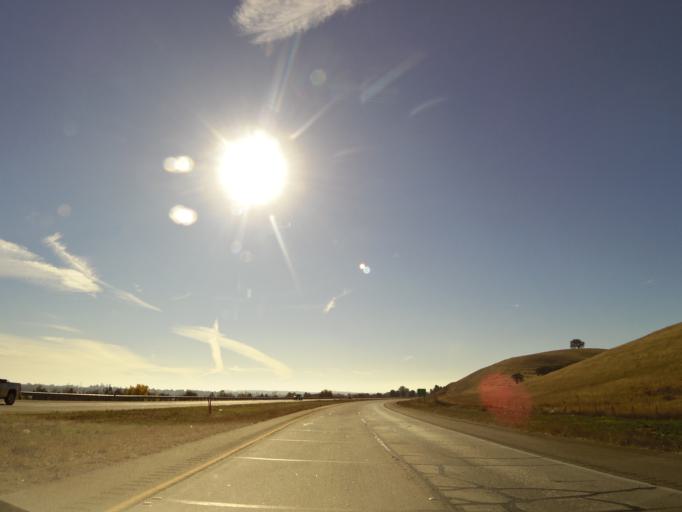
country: US
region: California
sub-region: San Luis Obispo County
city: San Miguel
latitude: 35.7631
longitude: -120.6996
